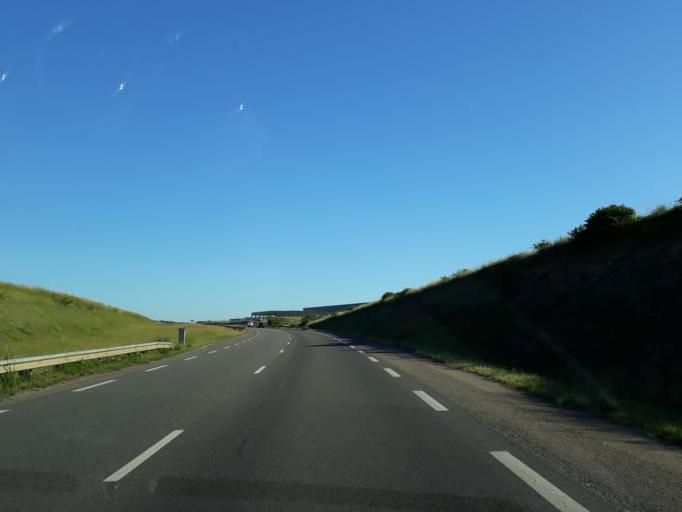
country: FR
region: Centre
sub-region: Departement du Cher
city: La Chapelle-Saint-Ursin
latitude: 47.0570
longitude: 2.3391
